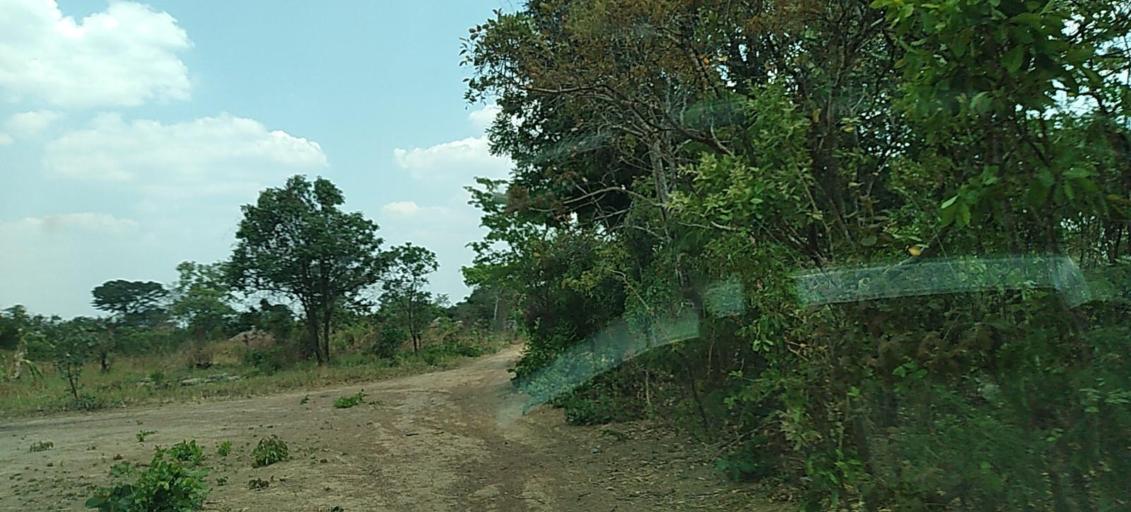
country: CD
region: Katanga
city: Kipushi
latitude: -11.9860
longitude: 27.4159
